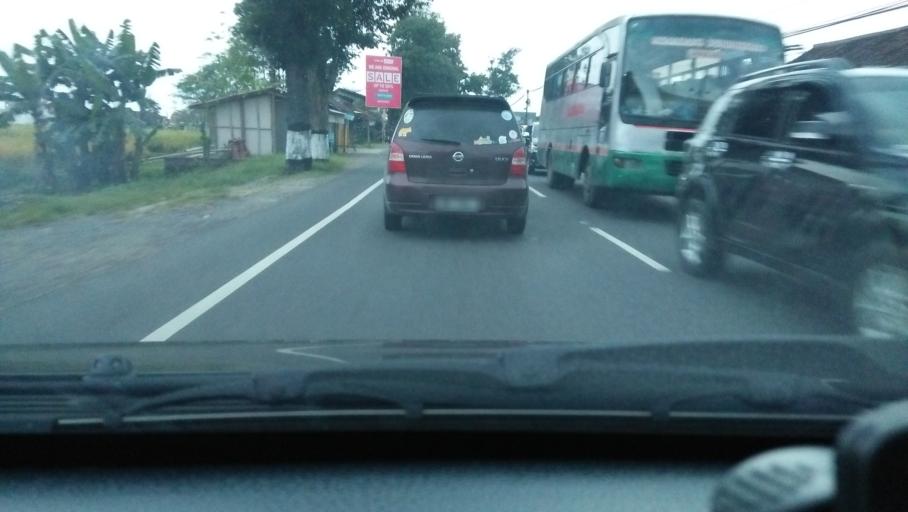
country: ID
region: Central Java
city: Magelang
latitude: -7.4308
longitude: 110.2291
